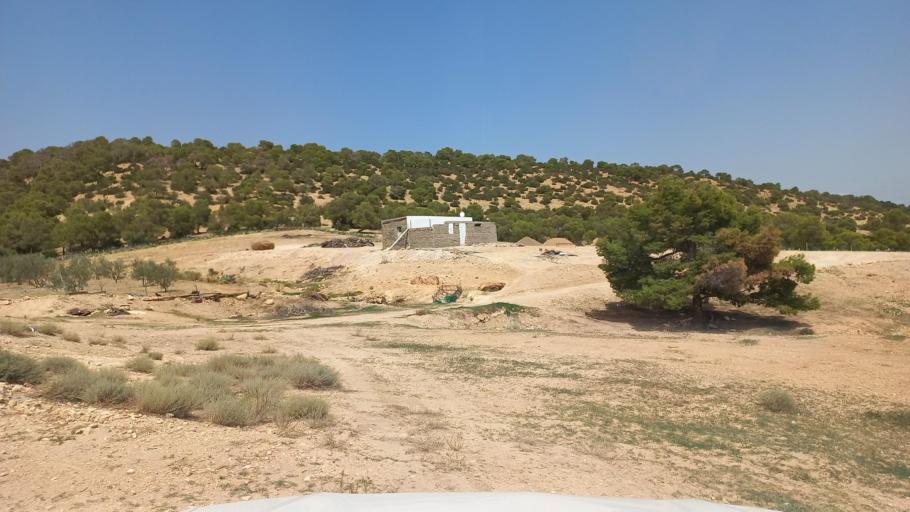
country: TN
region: Al Qasrayn
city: Kasserine
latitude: 35.3746
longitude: 8.8953
